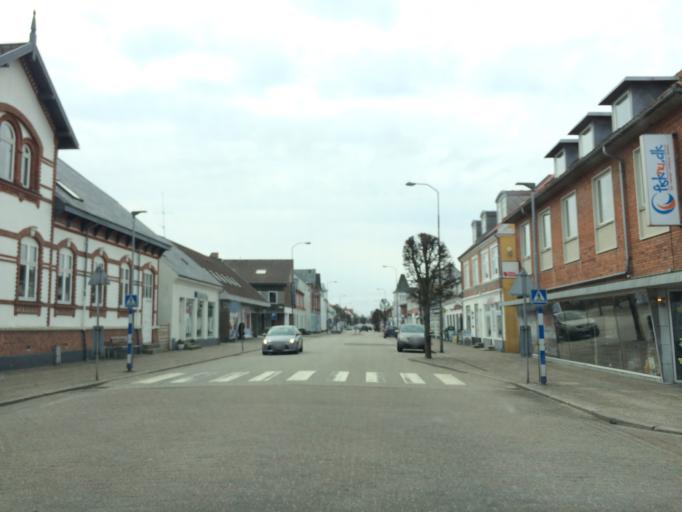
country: DK
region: Central Jutland
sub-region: Ringkobing-Skjern Kommune
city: Tarm
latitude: 55.9078
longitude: 8.5212
